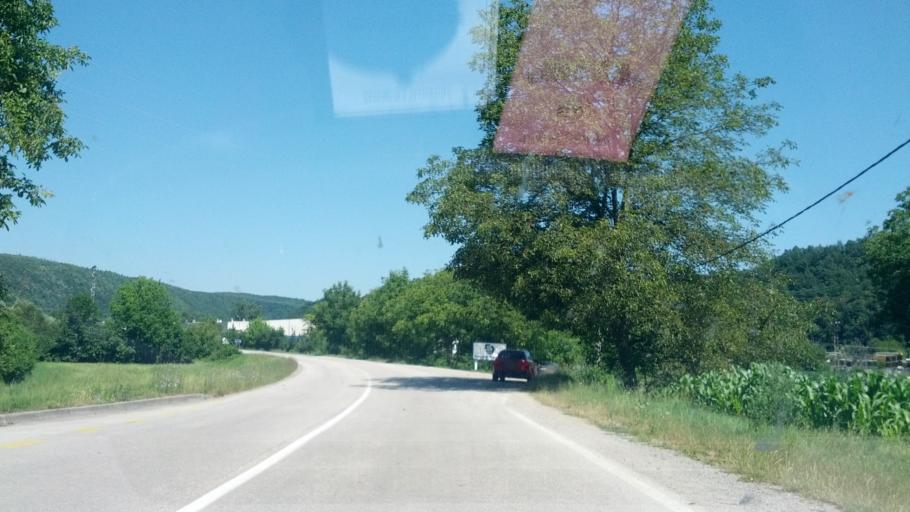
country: BA
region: Federation of Bosnia and Herzegovina
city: Bosanska Krupa
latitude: 44.9055
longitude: 16.1631
